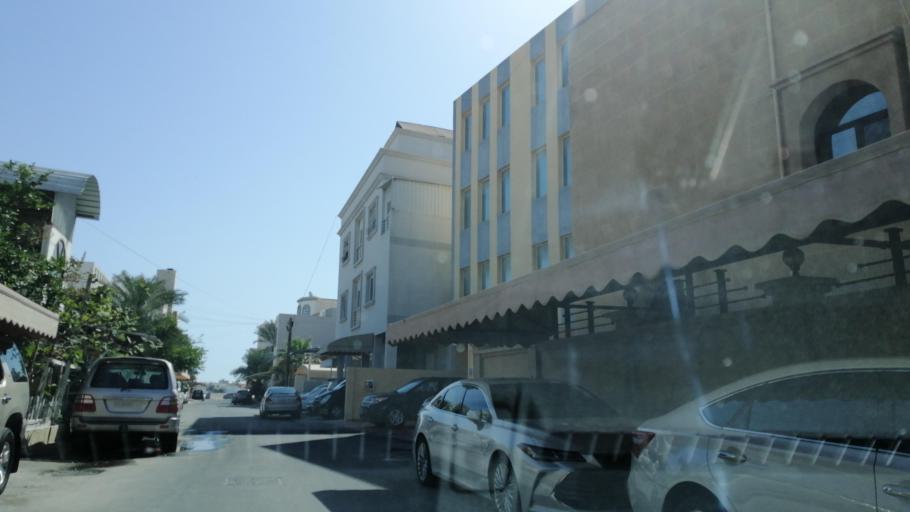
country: BH
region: Muharraq
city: Al Hadd
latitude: 26.2484
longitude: 50.6385
